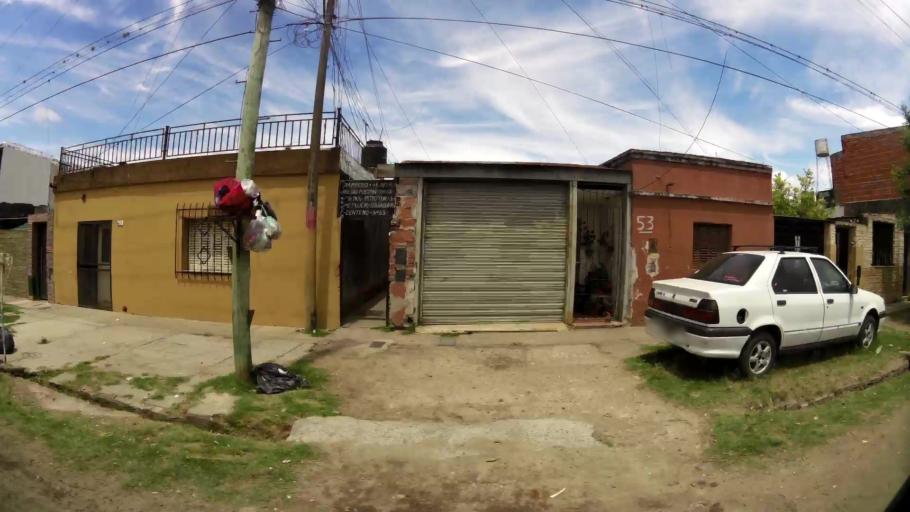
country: AR
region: Santa Fe
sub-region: Departamento de Rosario
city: Rosario
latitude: -32.9875
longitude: -60.6332
